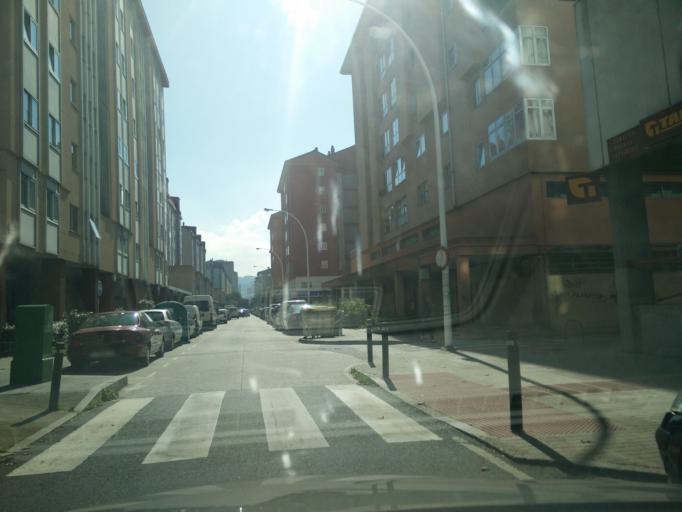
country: ES
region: Galicia
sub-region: Provincia da Coruna
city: A Coruna
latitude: 43.3503
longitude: -8.4065
